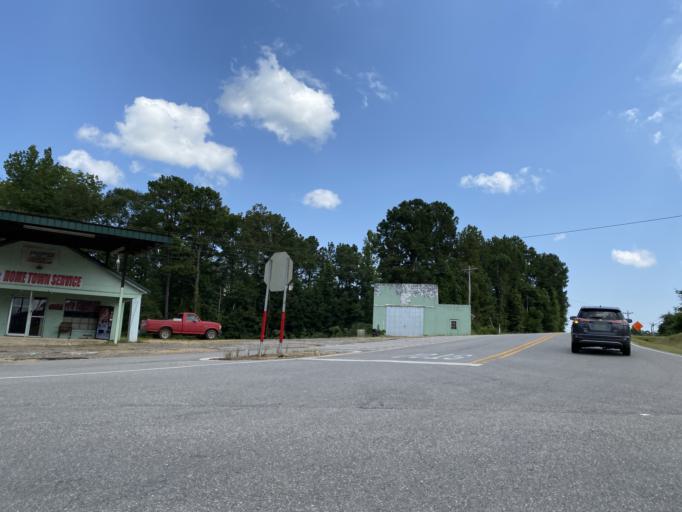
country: US
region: Alabama
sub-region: Wilcox County
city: Camden
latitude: 31.9943
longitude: -87.2808
